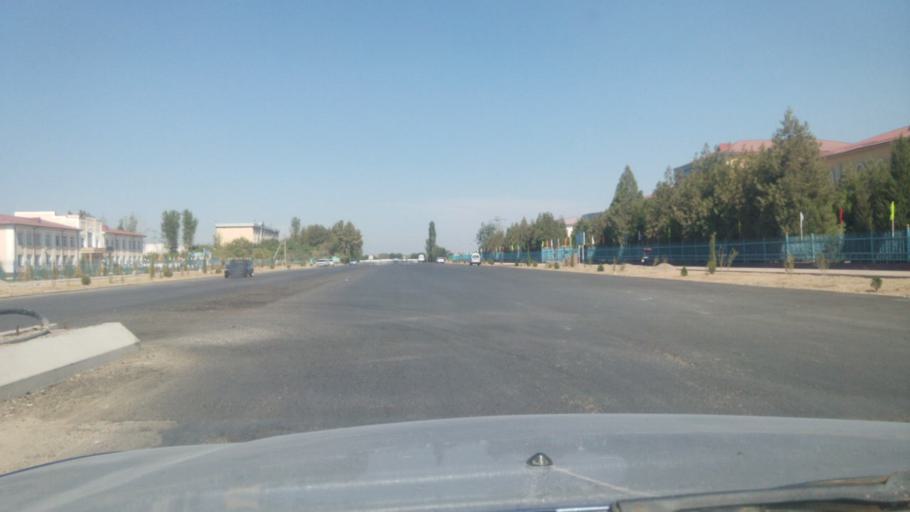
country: UZ
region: Sirdaryo
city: Guliston
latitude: 40.5158
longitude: 68.7886
